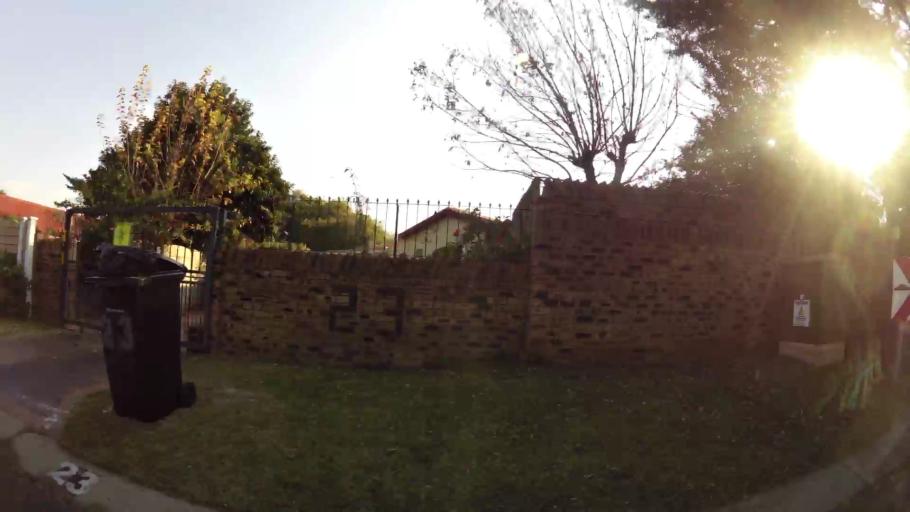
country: ZA
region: Gauteng
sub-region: City of Johannesburg Metropolitan Municipality
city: Modderfontein
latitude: -26.0822
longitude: 28.2058
